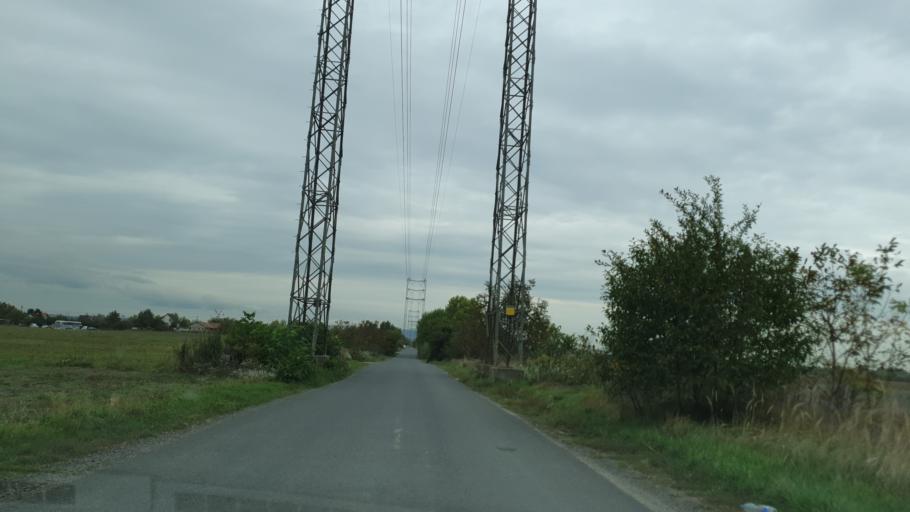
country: HU
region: Budapest
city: Budapest XXI. keruelet
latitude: 47.3906
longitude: 19.0708
